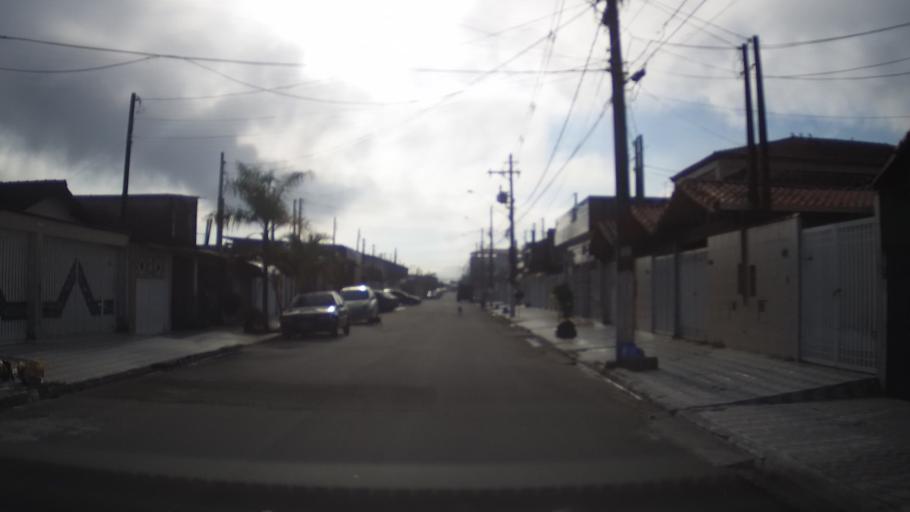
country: BR
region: Sao Paulo
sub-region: Praia Grande
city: Praia Grande
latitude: -24.0134
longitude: -46.4823
